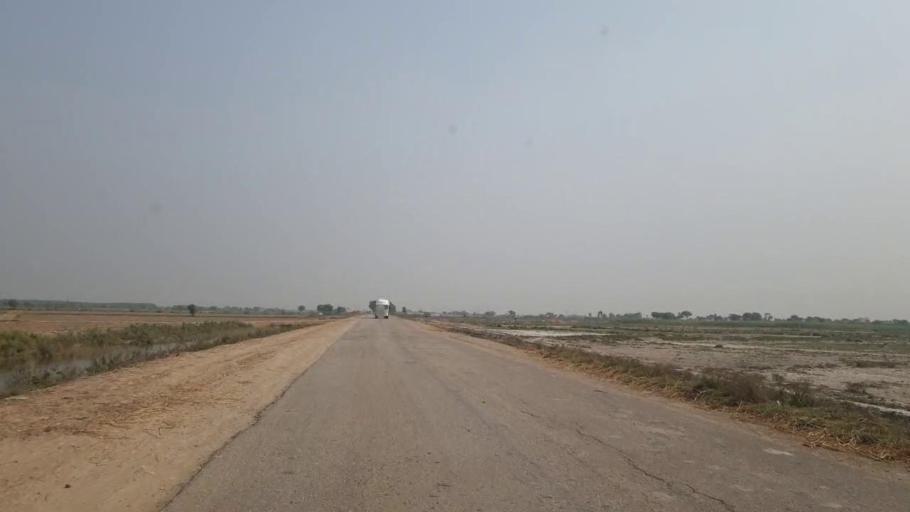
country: PK
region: Sindh
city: Matli
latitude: 25.0611
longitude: 68.6481
